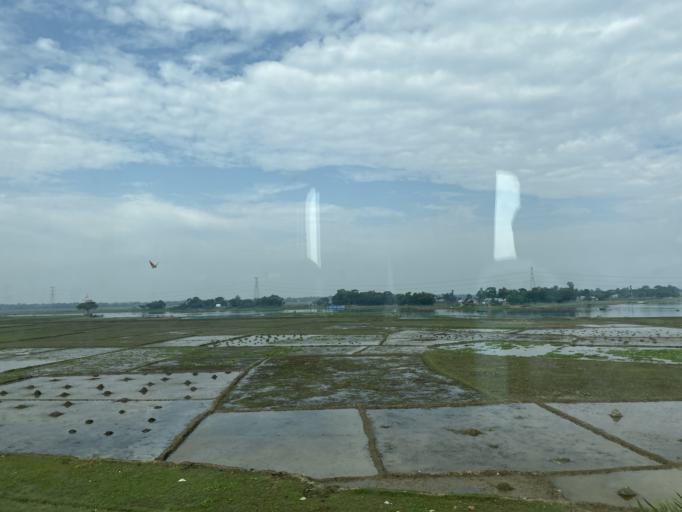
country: IN
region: Tripura
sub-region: West Tripura
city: Agartala
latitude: 23.8856
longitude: 91.2077
